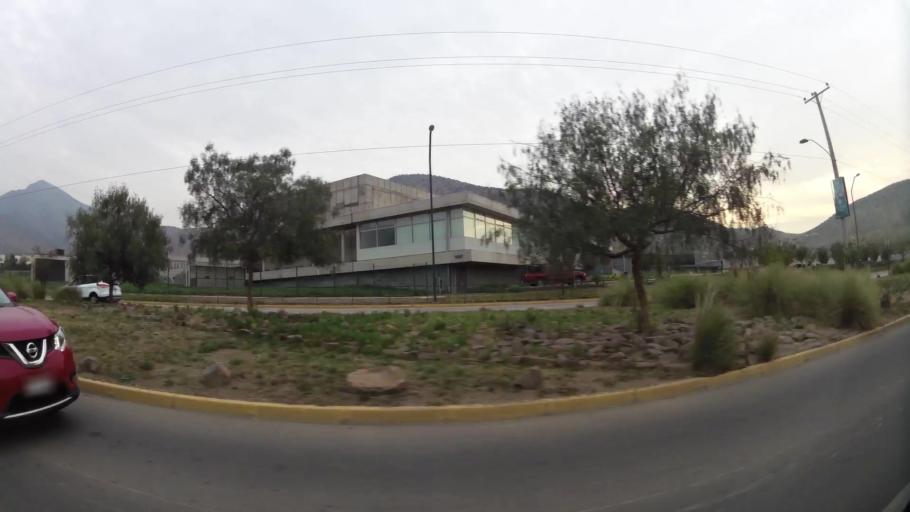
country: CL
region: Santiago Metropolitan
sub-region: Provincia de Chacabuco
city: Chicureo Abajo
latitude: -33.3187
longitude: -70.6519
